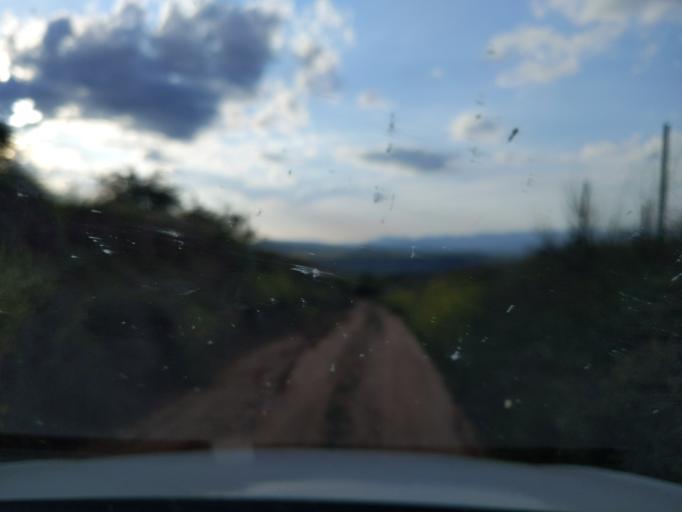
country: ES
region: La Rioja
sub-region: Provincia de La Rioja
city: Nalda
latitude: 42.3297
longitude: -2.4795
